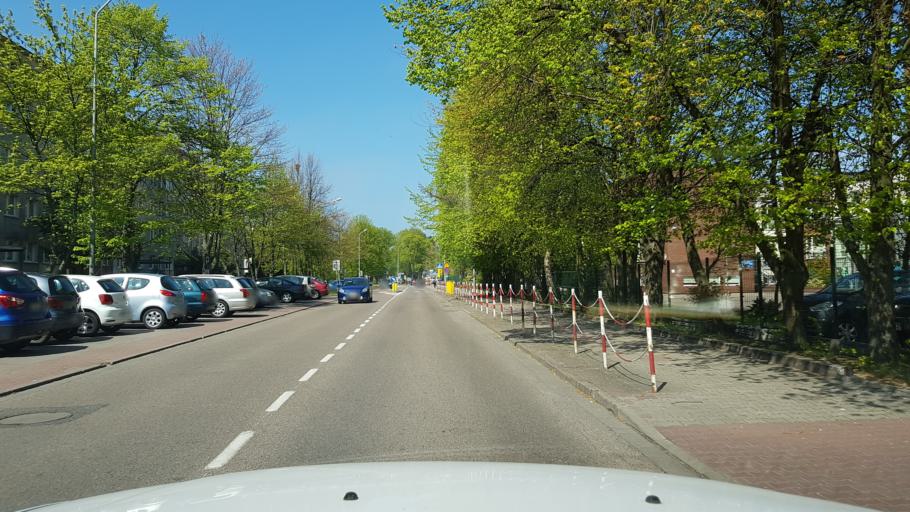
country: PL
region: Pomeranian Voivodeship
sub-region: Powiat slupski
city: Ustka
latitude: 54.5795
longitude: 16.8673
